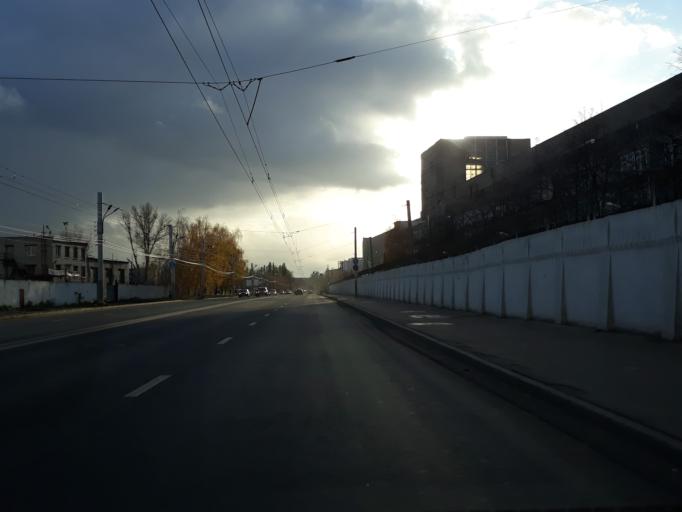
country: RU
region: Nizjnij Novgorod
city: Nizhniy Novgorod
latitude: 56.3218
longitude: 43.9093
